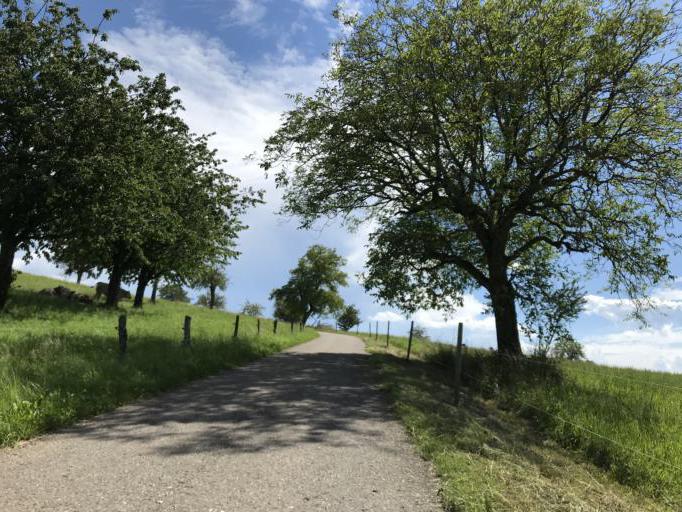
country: DE
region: Baden-Wuerttemberg
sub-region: Freiburg Region
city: Schopfheim
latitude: 47.6393
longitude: 7.8290
